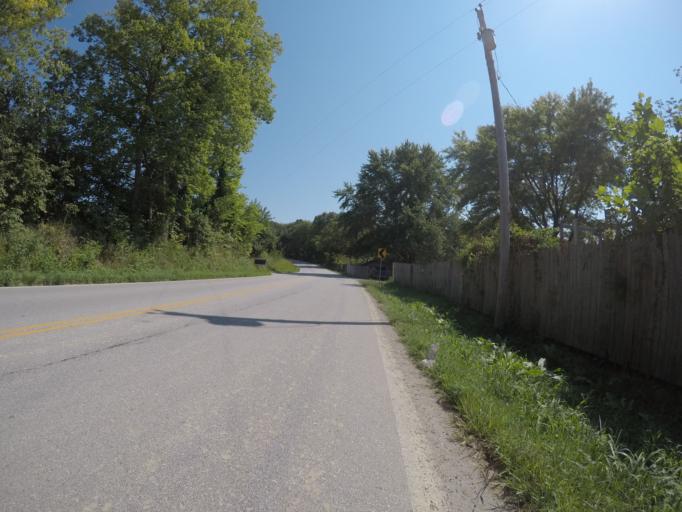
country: US
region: Kansas
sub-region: Leavenworth County
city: Lansing
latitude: 39.2131
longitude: -94.8400
